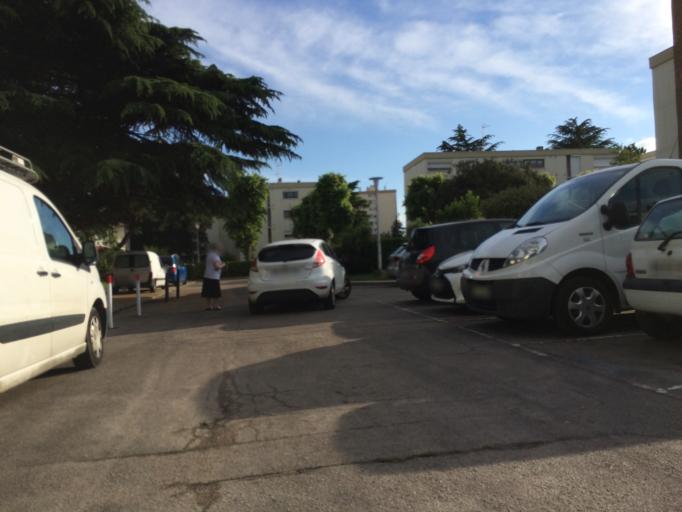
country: FR
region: Ile-de-France
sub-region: Departement de l'Essonne
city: Chilly-Mazarin
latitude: 48.7077
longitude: 2.3146
